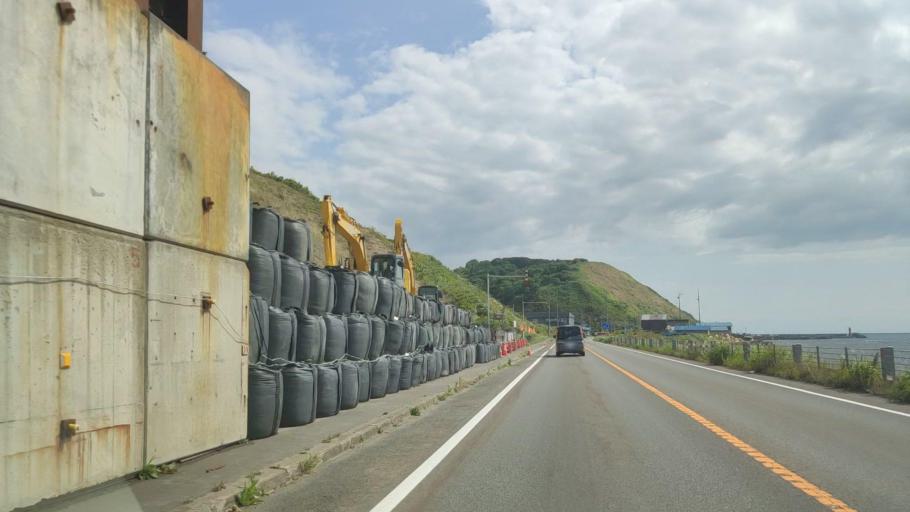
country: JP
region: Hokkaido
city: Rumoi
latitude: 44.2320
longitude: 141.6565
